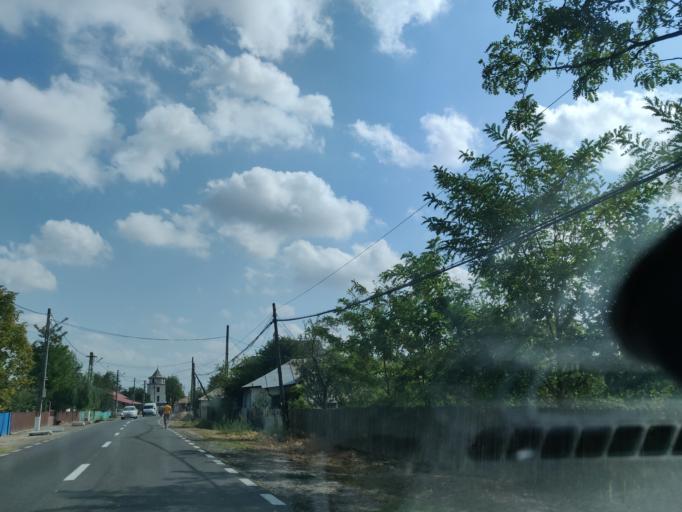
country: RO
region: Vrancea
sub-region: Comuna Ciorasti
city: Ciorasti
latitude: 45.4311
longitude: 27.3093
